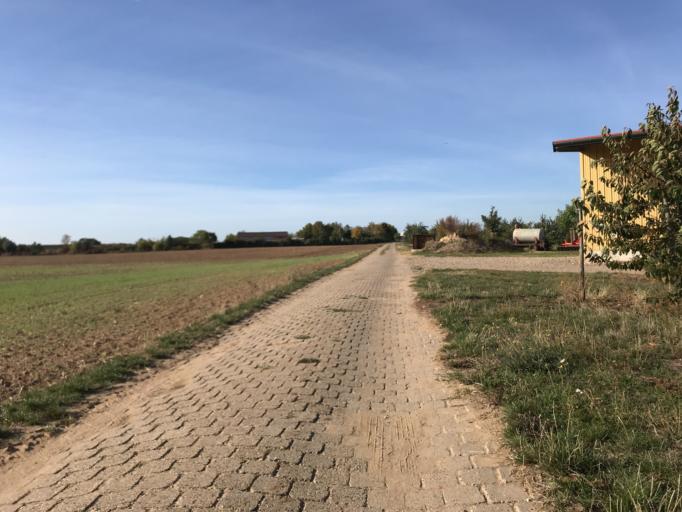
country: DE
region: Rheinland-Pfalz
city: Wackernheim
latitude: 49.9689
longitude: 8.1282
